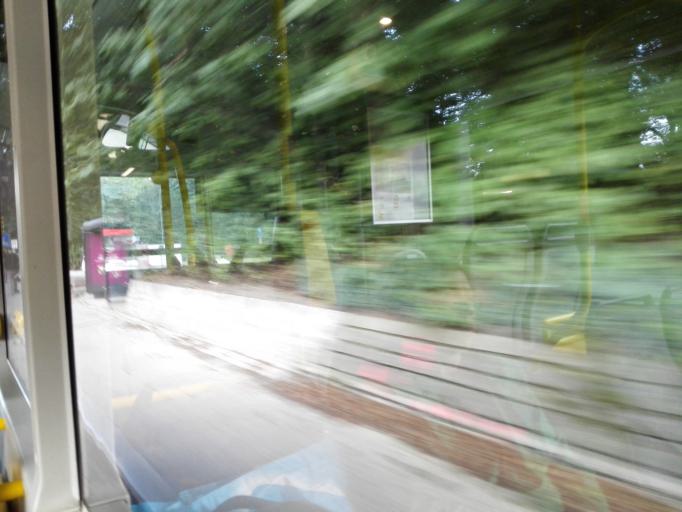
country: BE
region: Flanders
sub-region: Provincie Vlaams-Brabant
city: Tervuren
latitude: 50.8295
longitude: 4.5132
